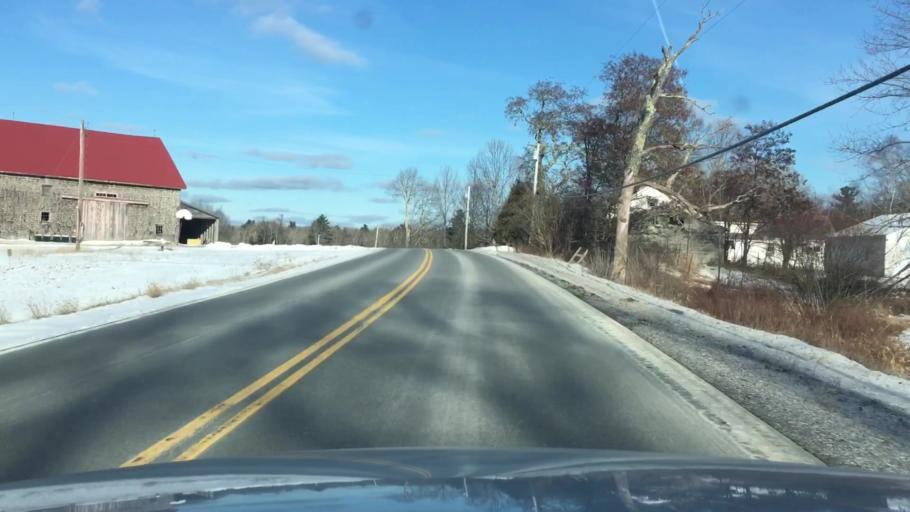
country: US
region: Maine
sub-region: Penobscot County
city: Holden
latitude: 44.7562
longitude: -68.5973
